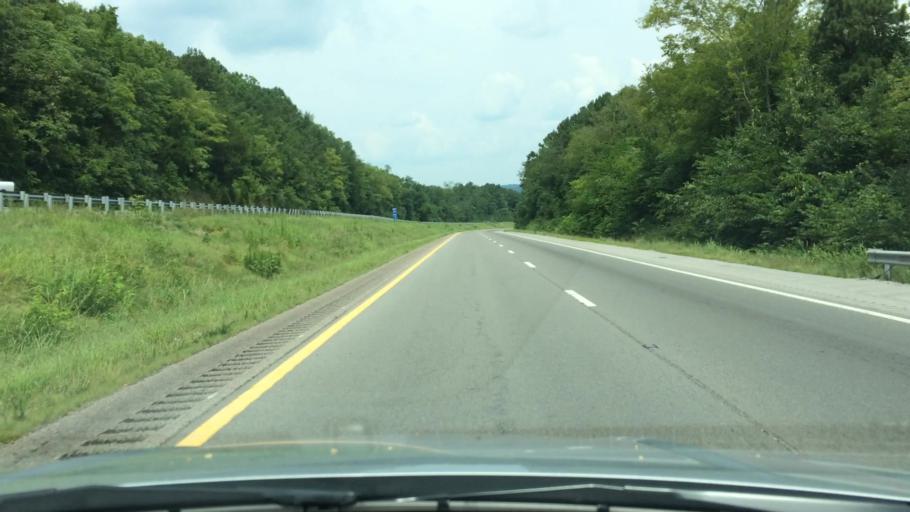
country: US
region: Tennessee
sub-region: Marshall County
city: Cornersville
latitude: 35.2651
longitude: -86.8871
